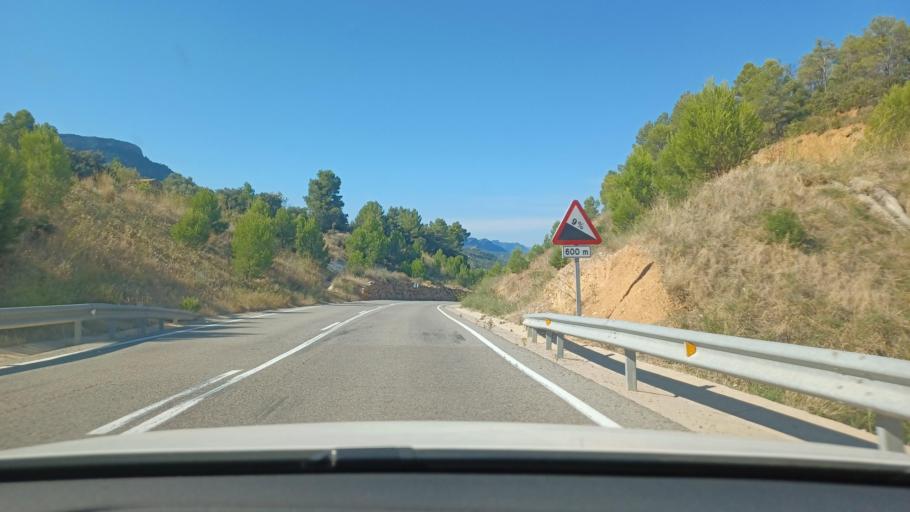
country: ES
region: Catalonia
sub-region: Provincia de Tarragona
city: Bot
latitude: 40.9640
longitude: 0.3652
